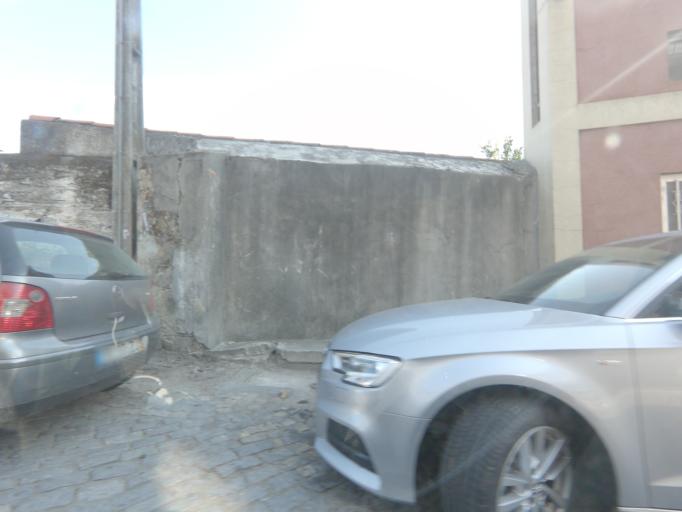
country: PT
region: Vila Real
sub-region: Sabrosa
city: Vilela
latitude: 41.1910
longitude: -7.5475
